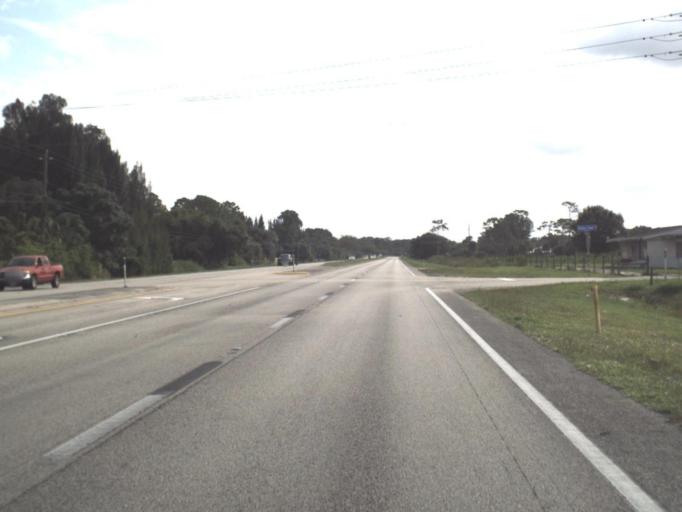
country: US
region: Florida
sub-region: Lee County
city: Olga
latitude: 26.7152
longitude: -81.6806
